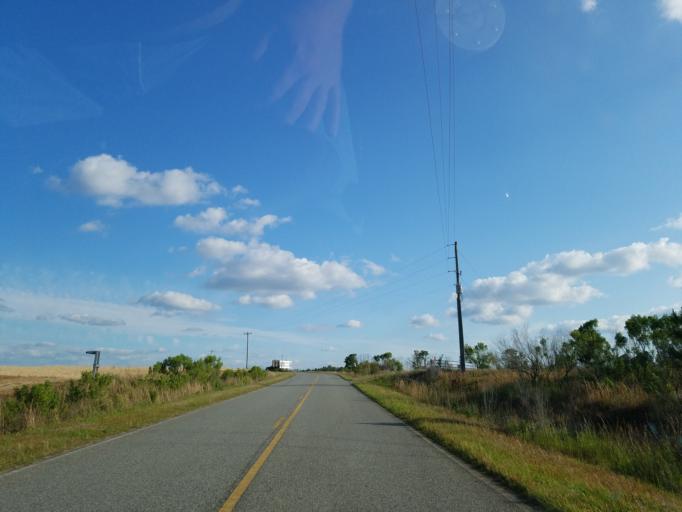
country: US
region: Georgia
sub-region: Turner County
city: Ashburn
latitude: 31.6189
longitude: -83.5677
